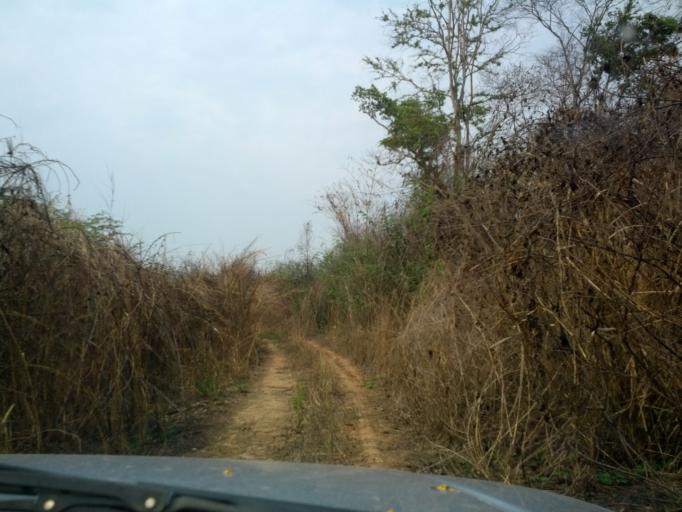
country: TH
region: Chiang Mai
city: Mae Taeng
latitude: 19.1091
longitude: 98.9835
